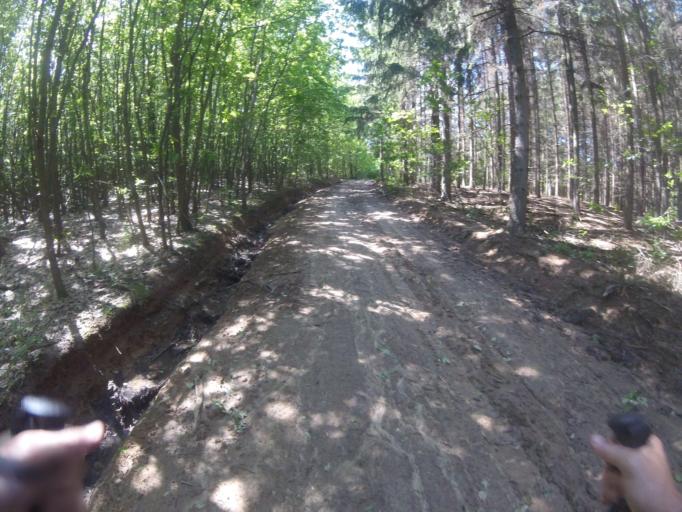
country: HU
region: Nograd
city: Matraverebely
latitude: 47.9362
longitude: 19.7933
